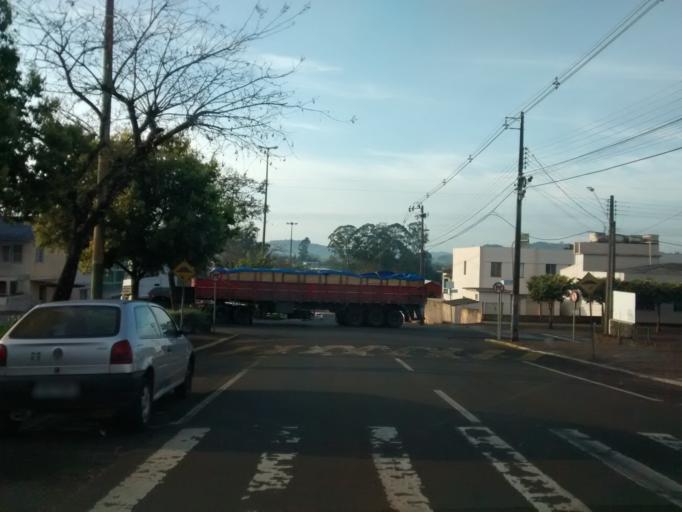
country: BR
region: Parana
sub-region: Francisco Beltrao
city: Francisco Beltrao
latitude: -26.1496
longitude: -53.0223
